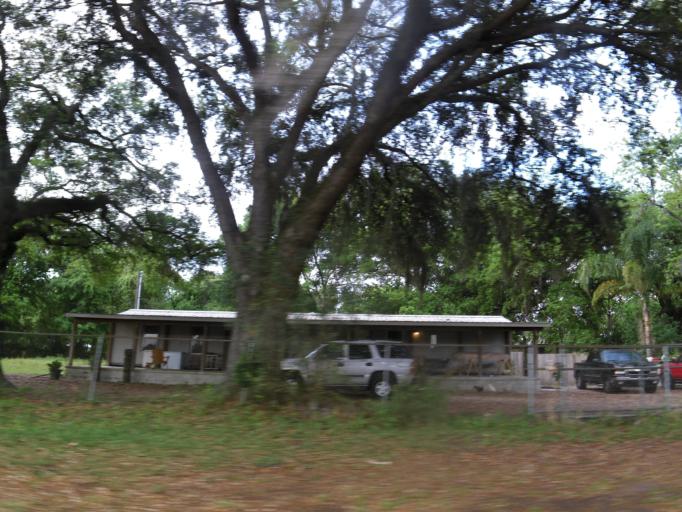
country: US
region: Florida
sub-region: Duval County
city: Jacksonville
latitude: 30.4619
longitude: -81.6358
